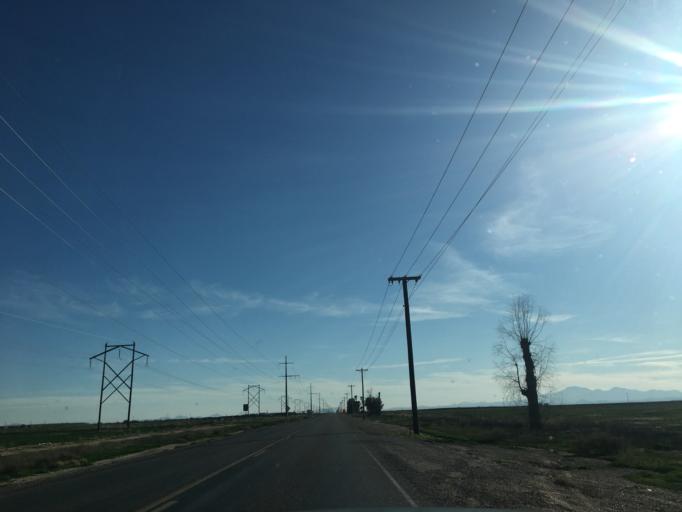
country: US
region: Arizona
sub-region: Pinal County
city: Maricopa
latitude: 33.0230
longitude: -111.9965
